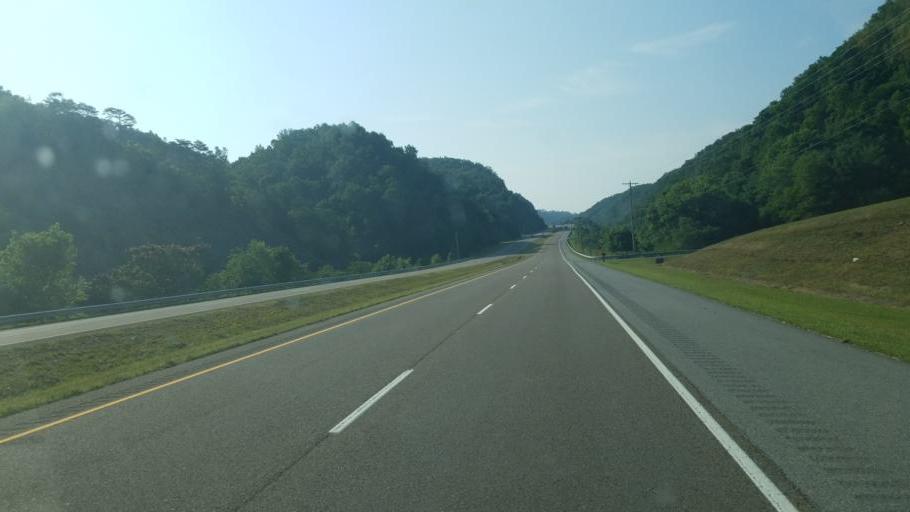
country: US
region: Tennessee
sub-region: Sullivan County
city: Bluff City
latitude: 36.4128
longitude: -82.2459
